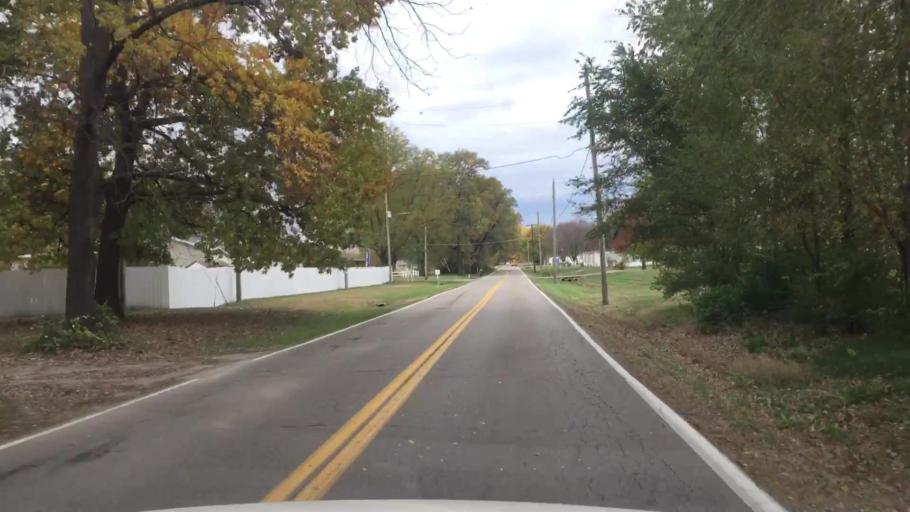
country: US
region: Kansas
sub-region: Shawnee County
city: Topeka
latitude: 39.0877
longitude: -95.6872
